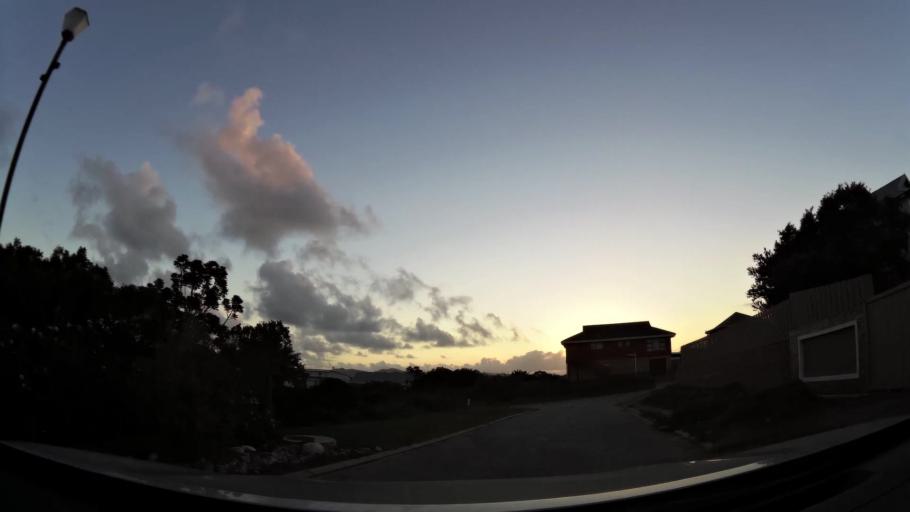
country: ZA
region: Western Cape
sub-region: Eden District Municipality
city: Knysna
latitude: -34.0255
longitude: 22.8091
